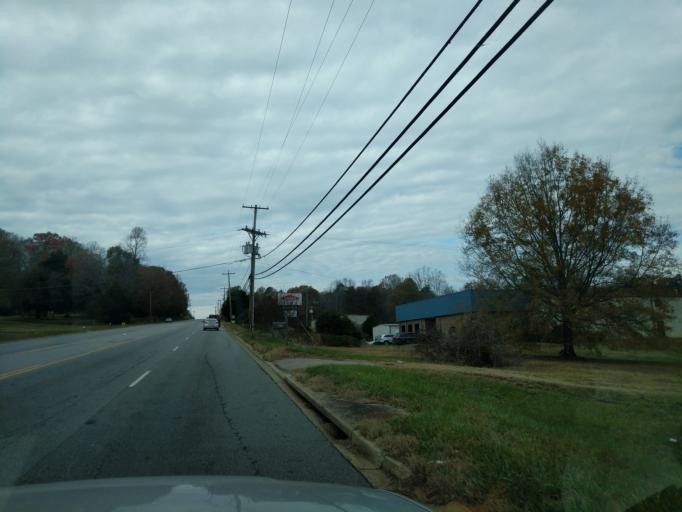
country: US
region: South Carolina
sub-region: Pickens County
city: Arial
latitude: 34.8381
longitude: -82.6300
